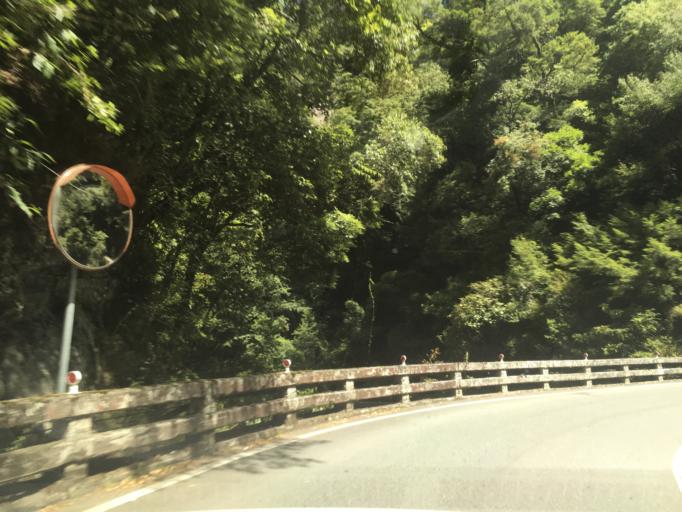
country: TW
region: Taiwan
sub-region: Nantou
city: Puli
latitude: 24.2126
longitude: 121.2650
